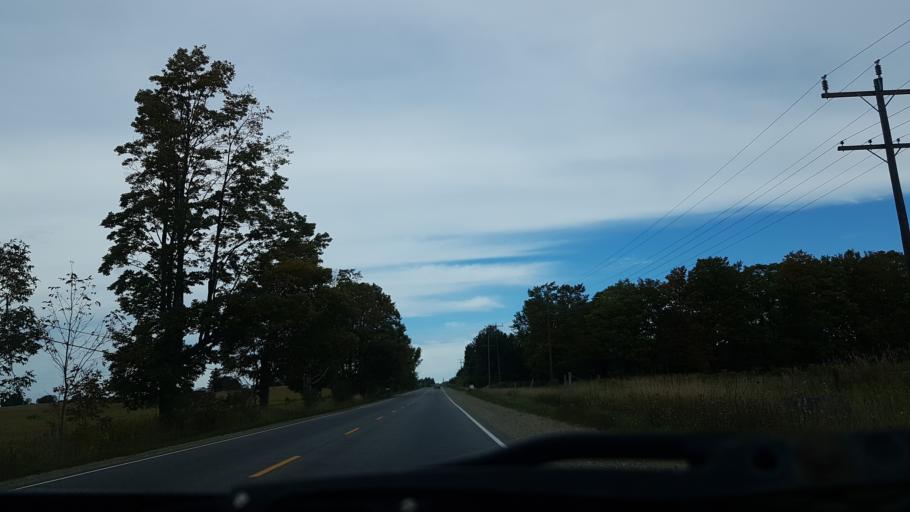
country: CA
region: Ontario
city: Wasaga Beach
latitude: 44.3450
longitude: -80.0800
